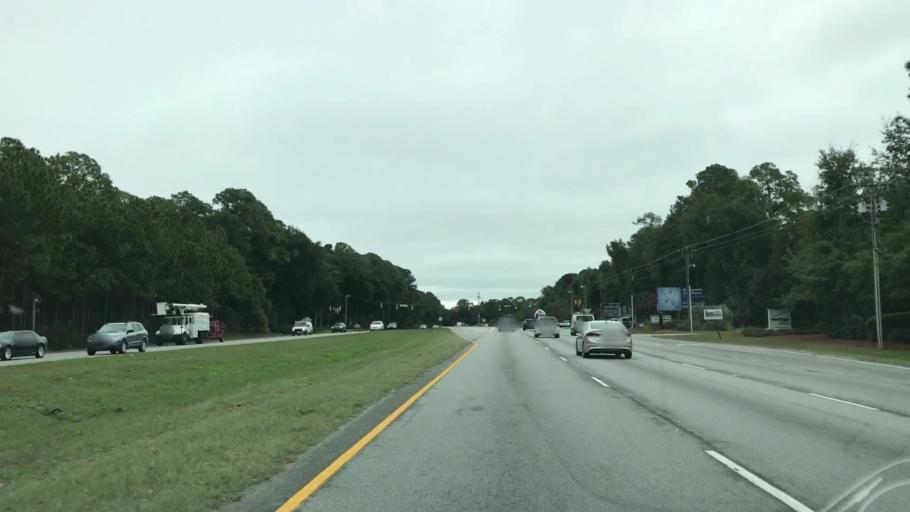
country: US
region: South Carolina
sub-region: Beaufort County
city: Bluffton
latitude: 32.2451
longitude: -80.8280
